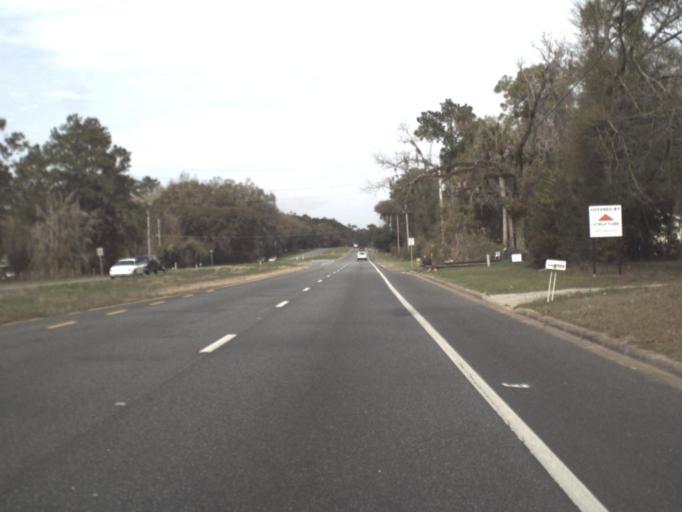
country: US
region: Florida
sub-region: Gadsden County
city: Midway
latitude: 30.4622
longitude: -84.3913
